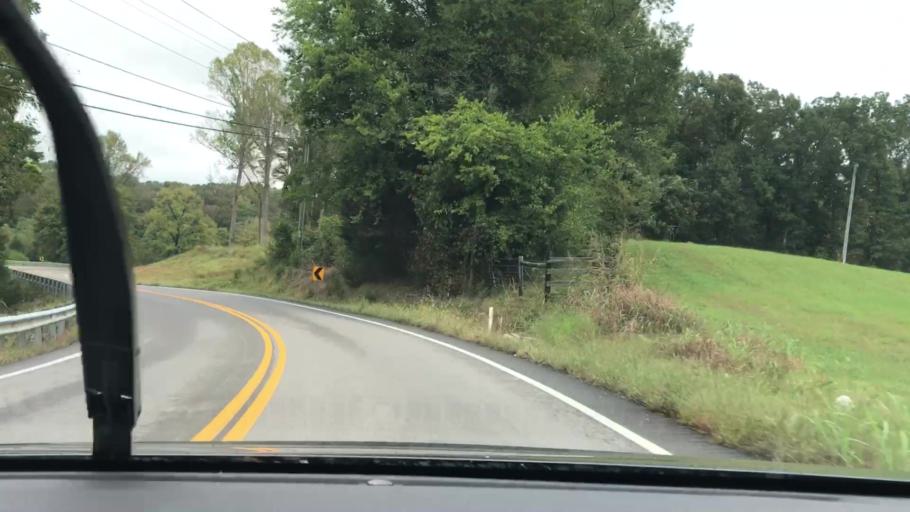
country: US
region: Kentucky
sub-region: Monroe County
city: Tompkinsville
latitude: 36.6370
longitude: -85.7671
